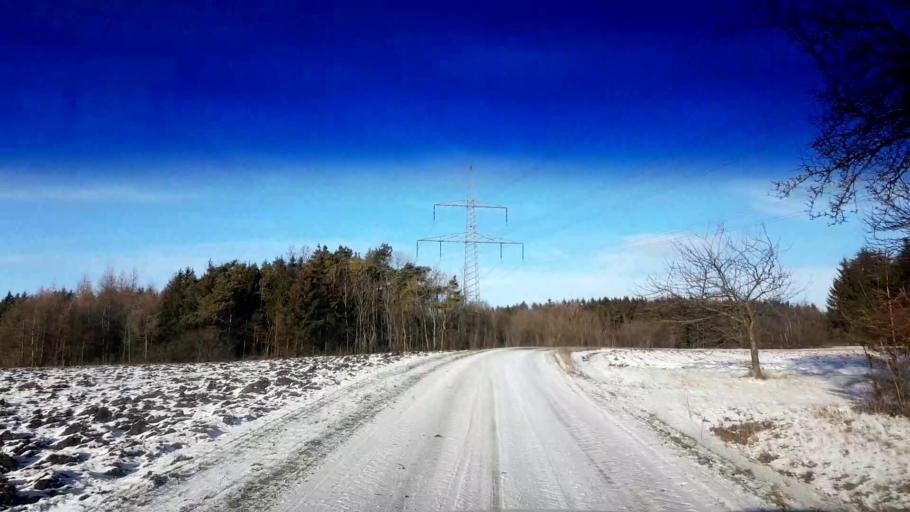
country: DE
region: Bavaria
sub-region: Upper Franconia
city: Heiligenstadt
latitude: 49.8430
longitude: 11.1039
